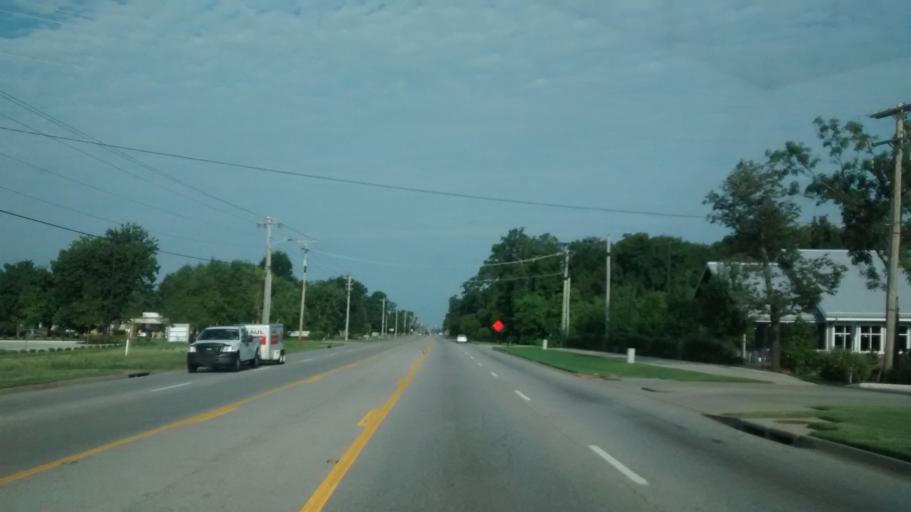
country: US
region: Arkansas
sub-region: Washington County
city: Farmington
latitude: 36.0786
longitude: -94.2102
